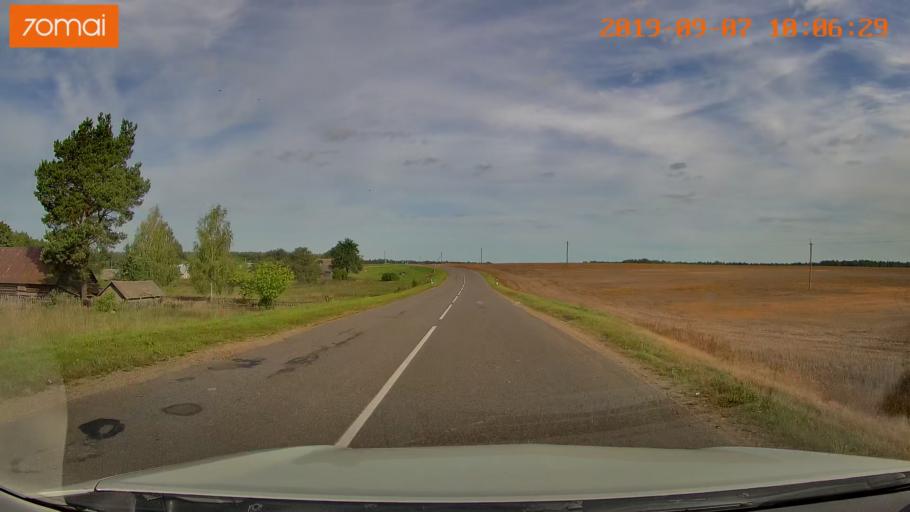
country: BY
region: Grodnenskaya
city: Voranava
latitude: 54.0624
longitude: 25.4031
